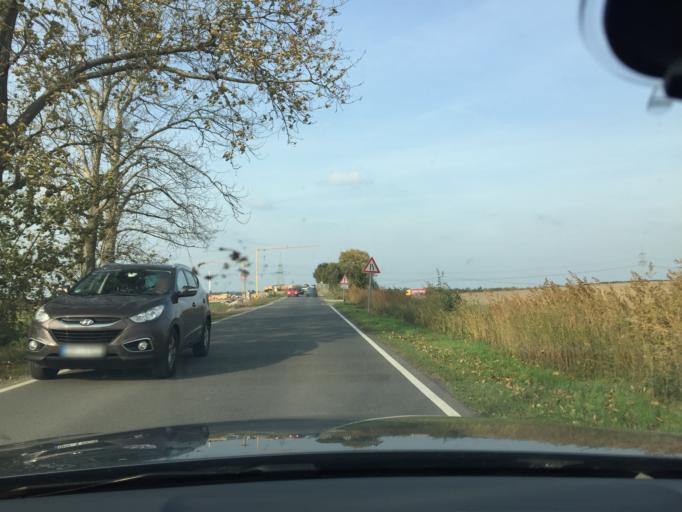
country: DE
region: Berlin
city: Buch
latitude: 52.6141
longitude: 13.5205
